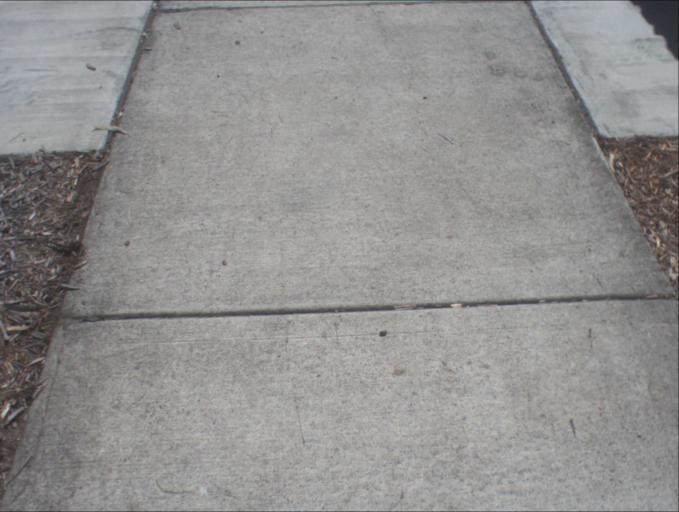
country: AU
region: Queensland
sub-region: Logan
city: Waterford West
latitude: -27.7136
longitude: 153.1445
